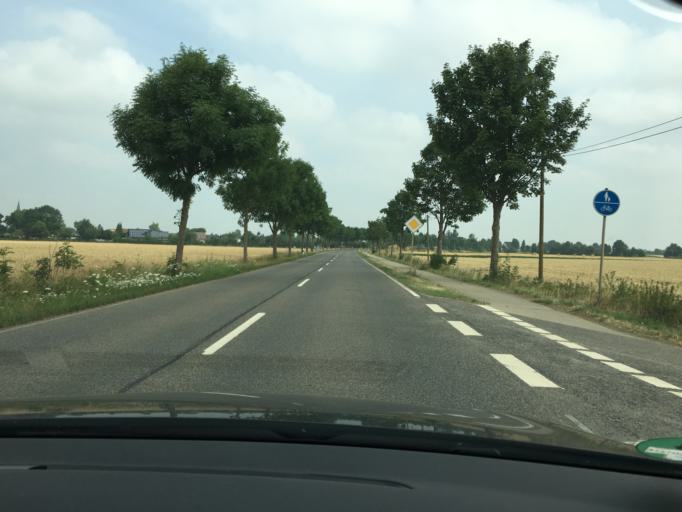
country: DE
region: North Rhine-Westphalia
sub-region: Regierungsbezirk Koln
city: Norvenich
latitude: 50.8054
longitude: 6.5872
